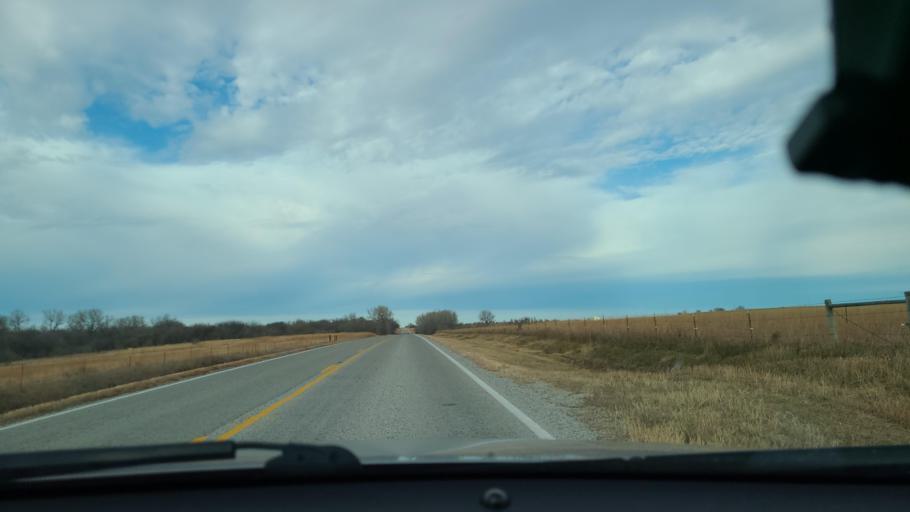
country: US
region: Kansas
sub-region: McPherson County
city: Inman
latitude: 38.3416
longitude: -97.9245
